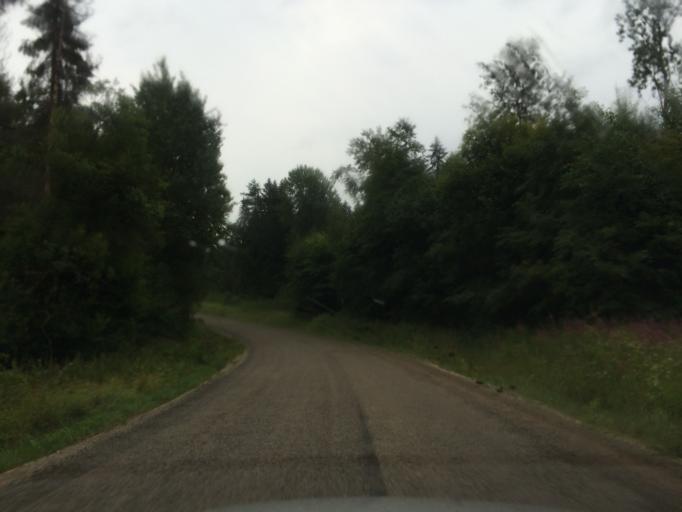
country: LV
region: Rezekne
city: Rezekne
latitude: 56.5717
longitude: 27.4742
